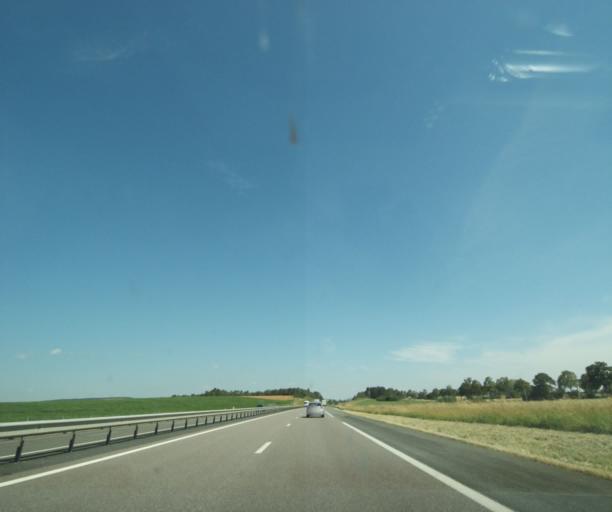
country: FR
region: Lorraine
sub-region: Departement de Meurthe-et-Moselle
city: Colombey-les-Belles
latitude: 48.5681
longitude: 5.8878
